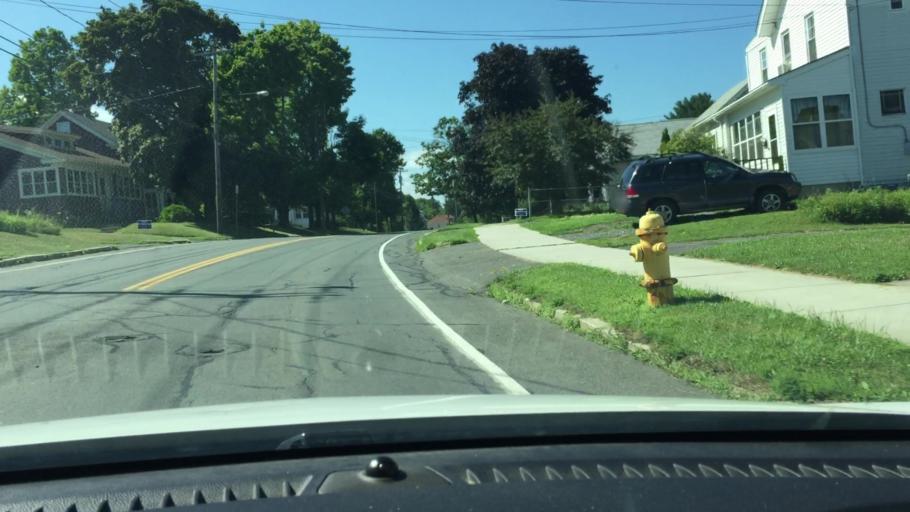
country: US
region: Massachusetts
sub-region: Berkshire County
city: Pittsfield
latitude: 42.4739
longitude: -73.2441
